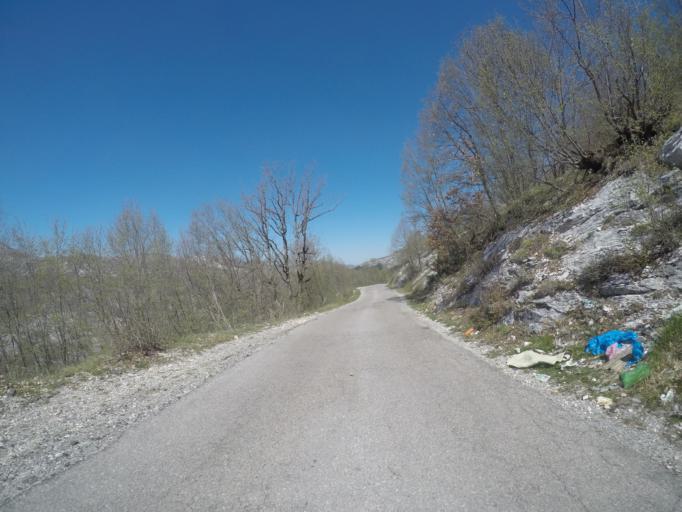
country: ME
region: Cetinje
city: Cetinje
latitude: 42.4508
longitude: 18.8740
